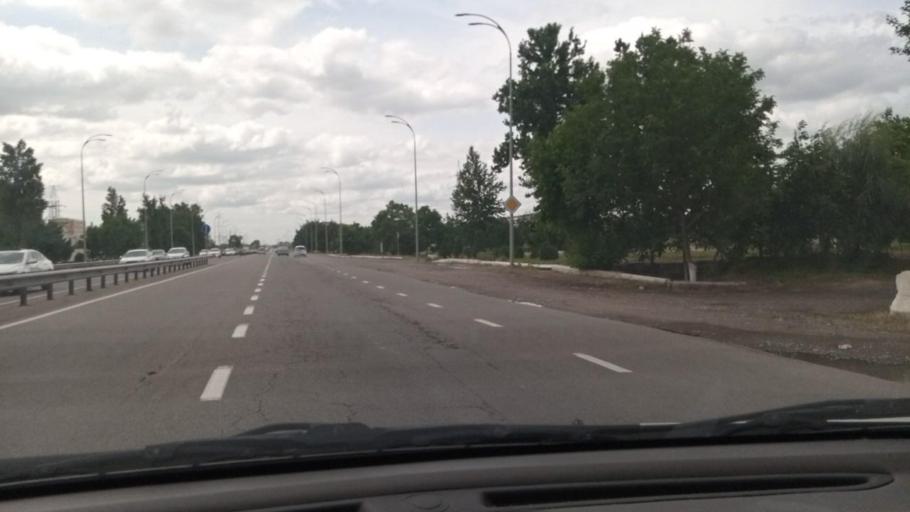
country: UZ
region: Toshkent Shahri
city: Bektemir
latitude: 41.2525
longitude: 69.3863
